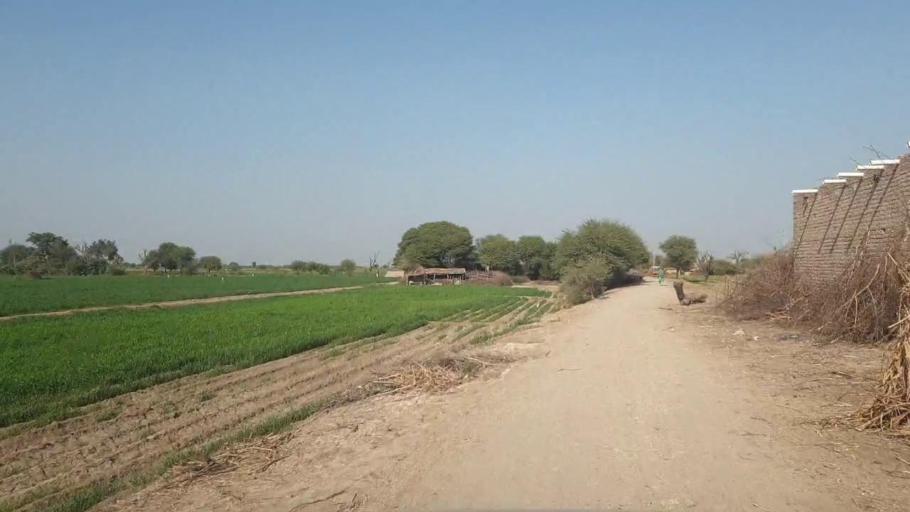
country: PK
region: Sindh
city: Chambar
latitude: 25.3196
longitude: 68.8395
